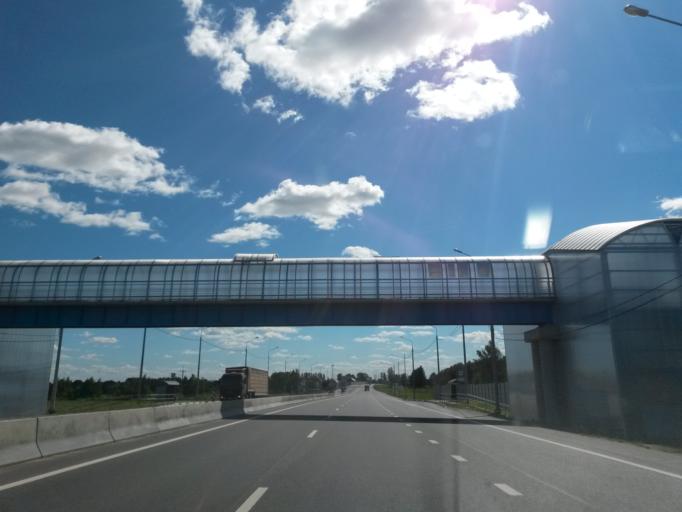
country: RU
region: Jaroslavl
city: Yaroslavl
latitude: 57.7185
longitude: 39.9025
